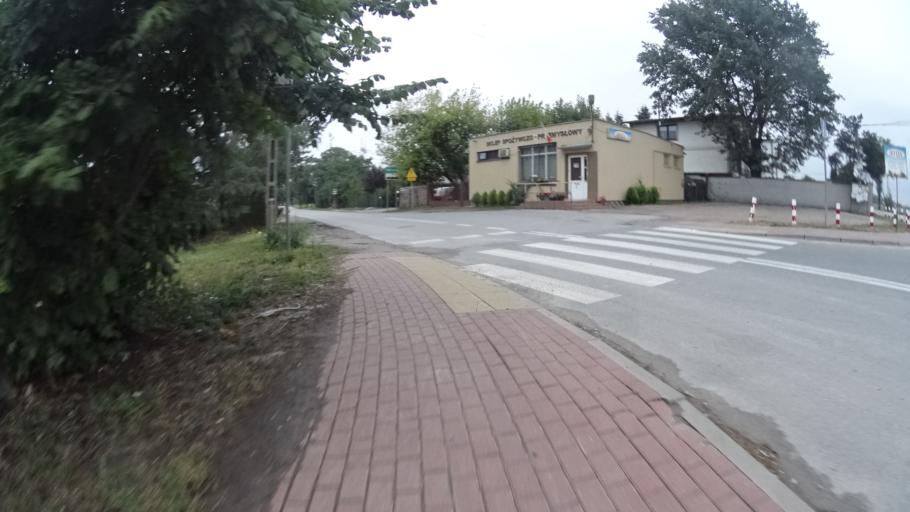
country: PL
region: Masovian Voivodeship
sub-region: Powiat warszawski zachodni
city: Stare Babice
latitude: 52.2314
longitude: 20.8234
